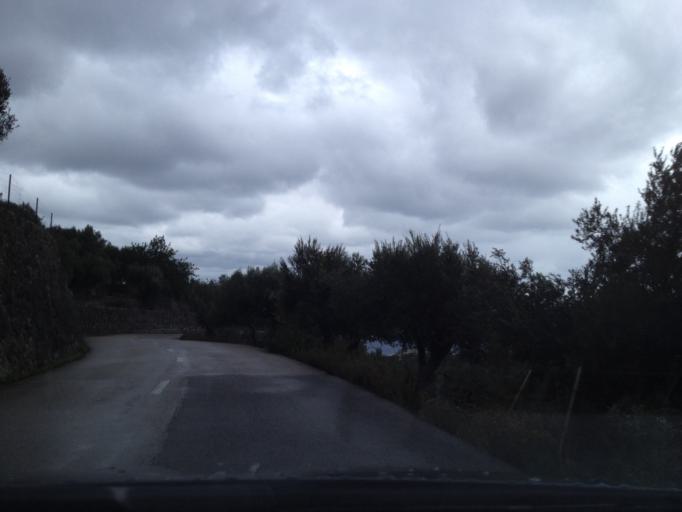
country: ES
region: Balearic Islands
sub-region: Illes Balears
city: Deia
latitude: 39.7743
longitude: 2.6755
